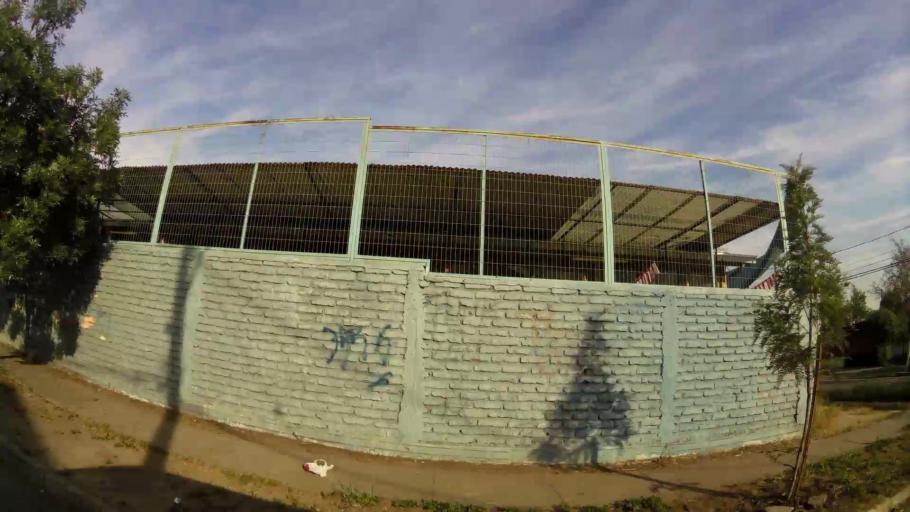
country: CL
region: Santiago Metropolitan
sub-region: Provincia de Santiago
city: Santiago
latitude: -33.5187
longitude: -70.6671
